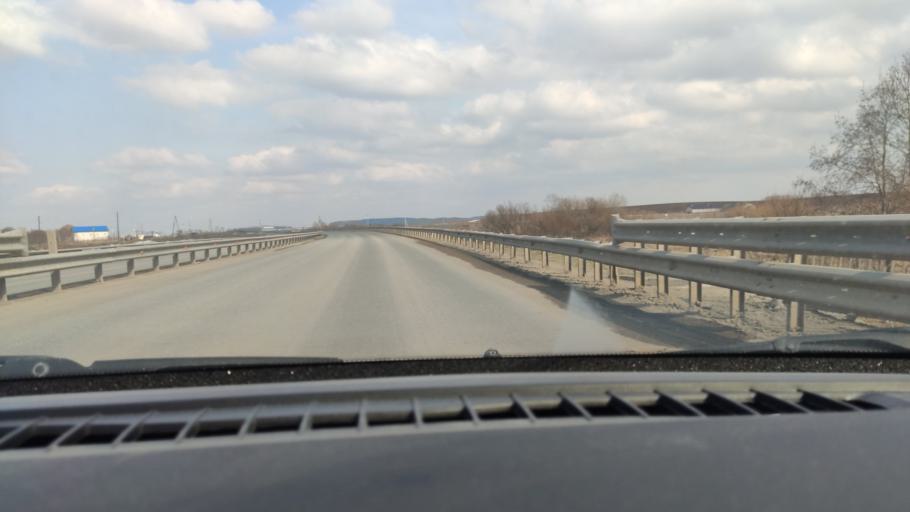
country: RU
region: Perm
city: Kultayevo
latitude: 57.8868
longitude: 55.9362
